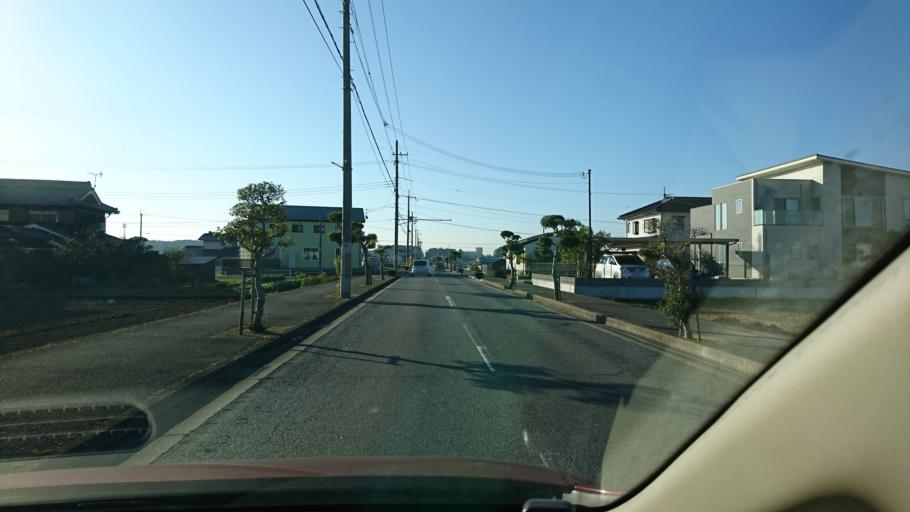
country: JP
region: Hyogo
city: Miki
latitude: 34.7602
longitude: 134.9199
